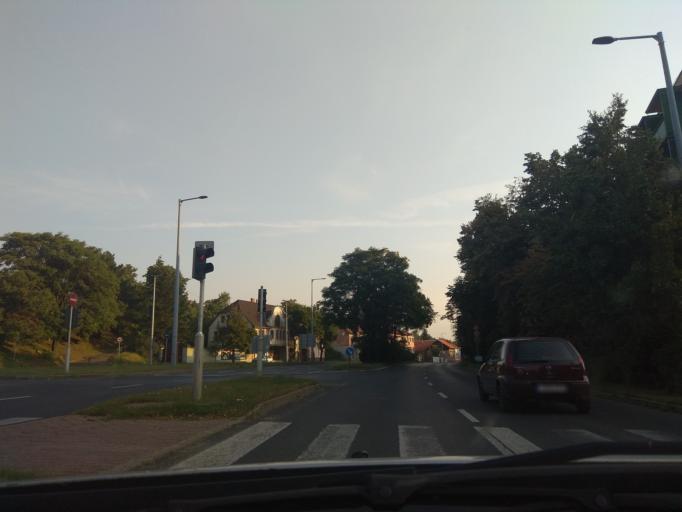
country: HU
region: Borsod-Abauj-Zemplen
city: Miskolc
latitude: 48.1093
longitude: 20.7883
